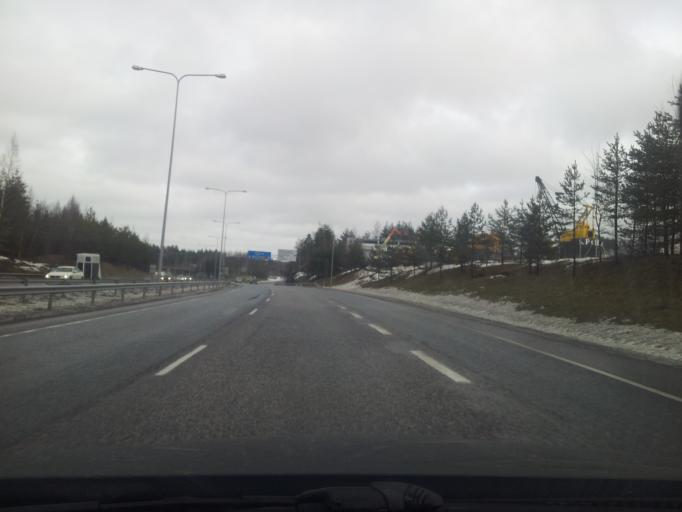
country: FI
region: Uusimaa
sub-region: Helsinki
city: Espoo
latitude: 60.2071
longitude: 24.6271
